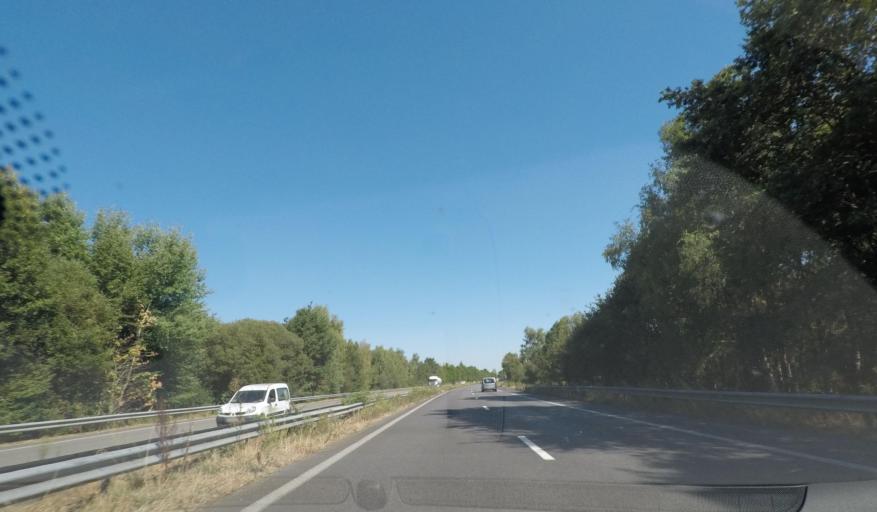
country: FR
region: Pays de la Loire
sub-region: Departement de la Loire-Atlantique
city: Missillac
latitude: 47.4704
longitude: -2.1651
